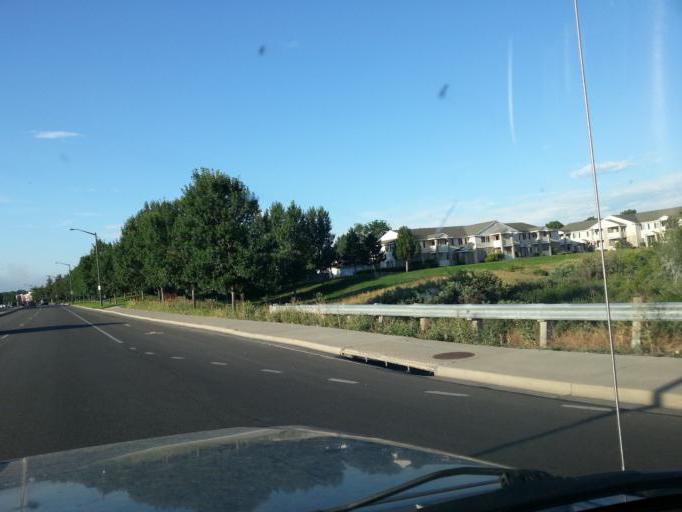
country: US
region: Colorado
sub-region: Larimer County
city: Loveland
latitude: 40.3855
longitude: -105.0972
